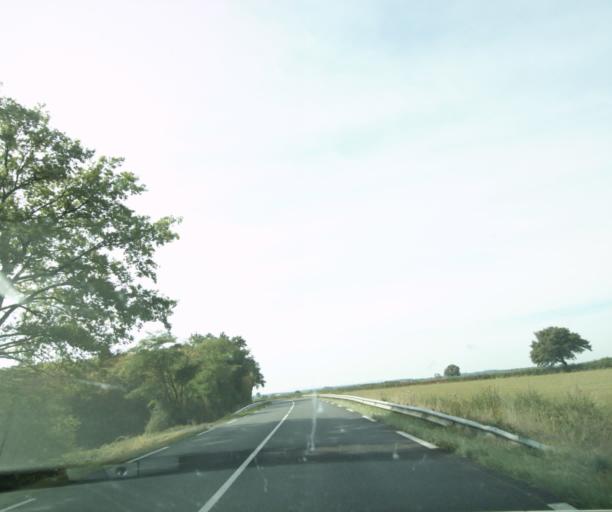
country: FR
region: Auvergne
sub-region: Departement de l'Allier
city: Saint-Francois
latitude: 46.4380
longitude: 3.9085
